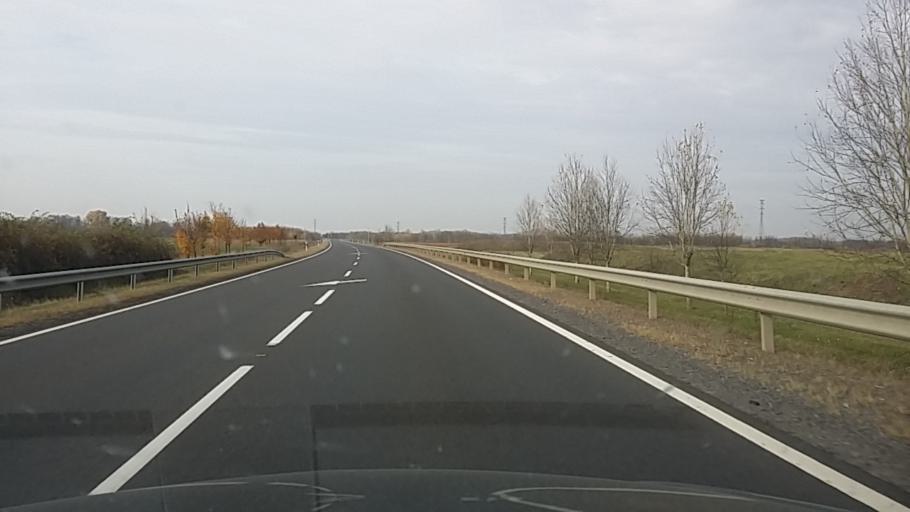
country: HU
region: Szabolcs-Szatmar-Bereg
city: Nyirpazony
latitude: 47.9538
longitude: 21.8202
